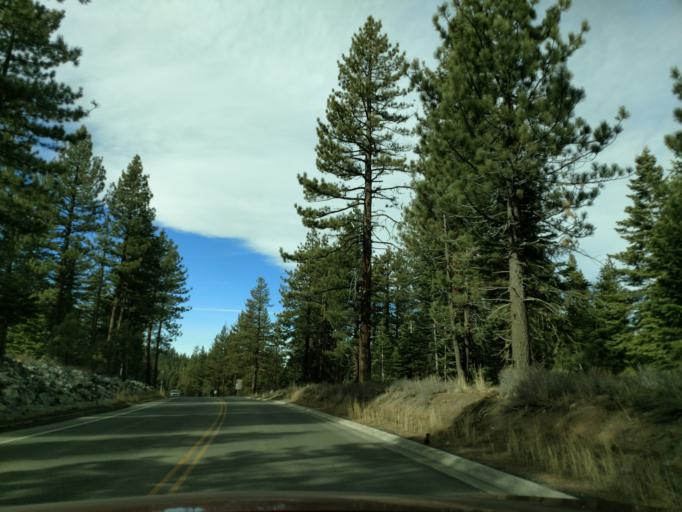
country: US
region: Nevada
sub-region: Douglas County
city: Kingsbury
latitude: 39.1049
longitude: -119.9169
